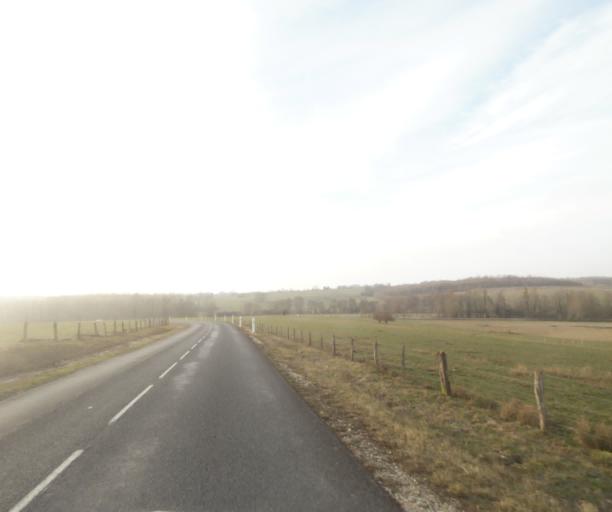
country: FR
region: Champagne-Ardenne
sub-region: Departement de la Marne
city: Sermaize-les-Bains
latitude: 48.7480
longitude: 4.9042
